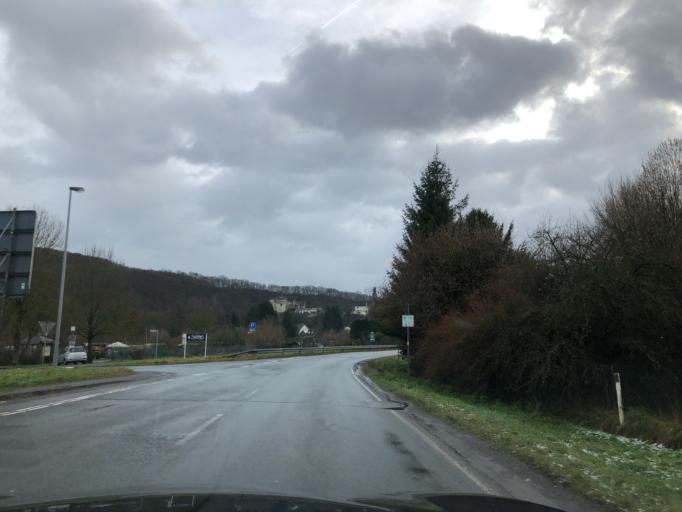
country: DE
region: Hesse
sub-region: Regierungsbezirk Giessen
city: Lohnberg
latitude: 50.5161
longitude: 8.2736
